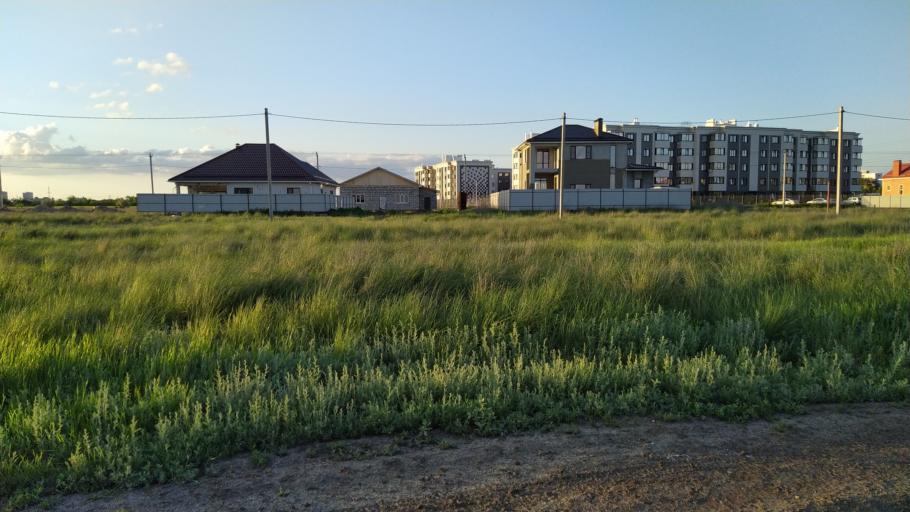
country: RU
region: Rostov
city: Bataysk
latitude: 47.1266
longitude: 39.7286
